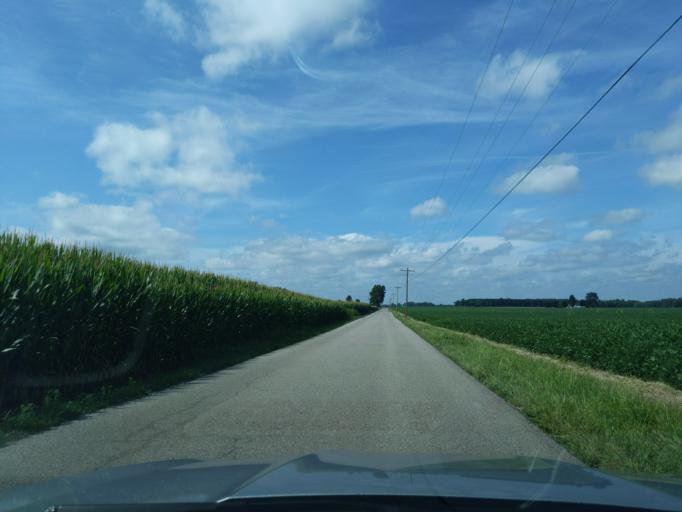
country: US
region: Indiana
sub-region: Ripley County
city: Batesville
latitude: 39.2809
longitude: -85.3476
